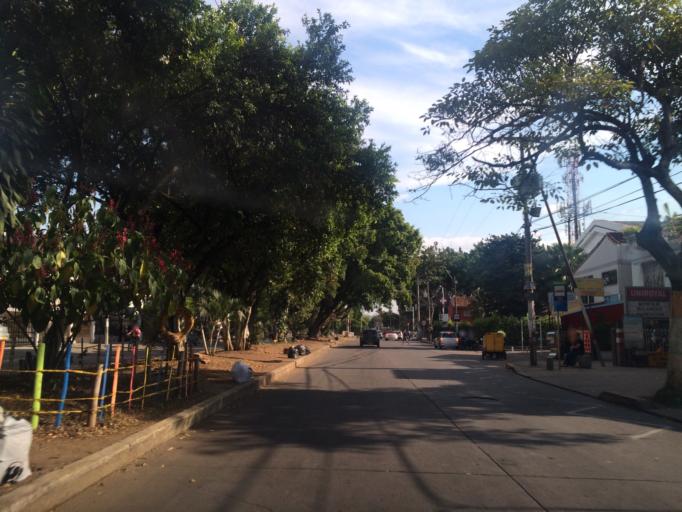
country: CO
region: Valle del Cauca
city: Cali
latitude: 3.4102
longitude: -76.5341
